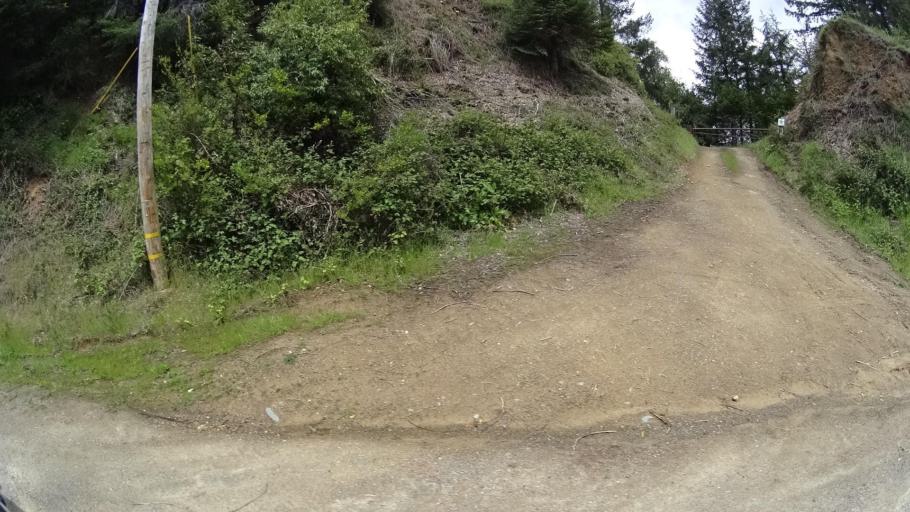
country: US
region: California
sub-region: Humboldt County
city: Blue Lake
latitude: 40.7668
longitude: -123.9292
